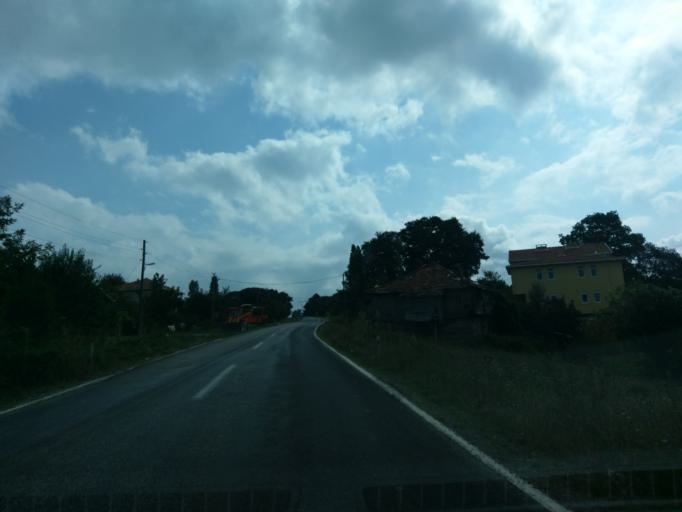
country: TR
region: Sinop
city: Erfelek
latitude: 41.9465
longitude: 34.7882
